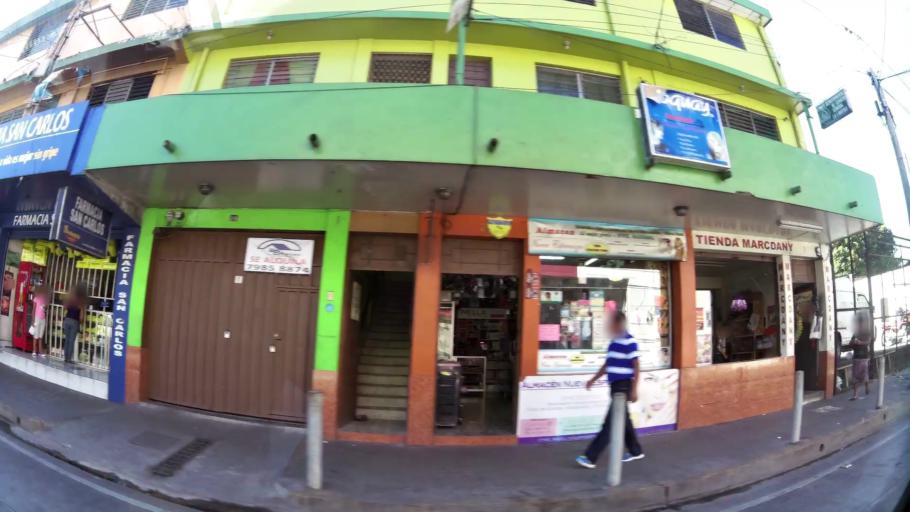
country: SV
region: La Libertad
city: Santa Tecla
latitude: 13.6732
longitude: -89.2898
